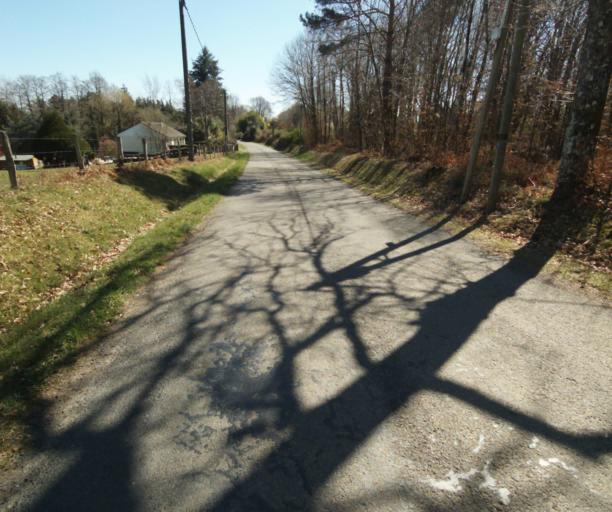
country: FR
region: Limousin
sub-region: Departement de la Correze
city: Saint-Clement
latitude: 45.3064
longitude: 1.6905
